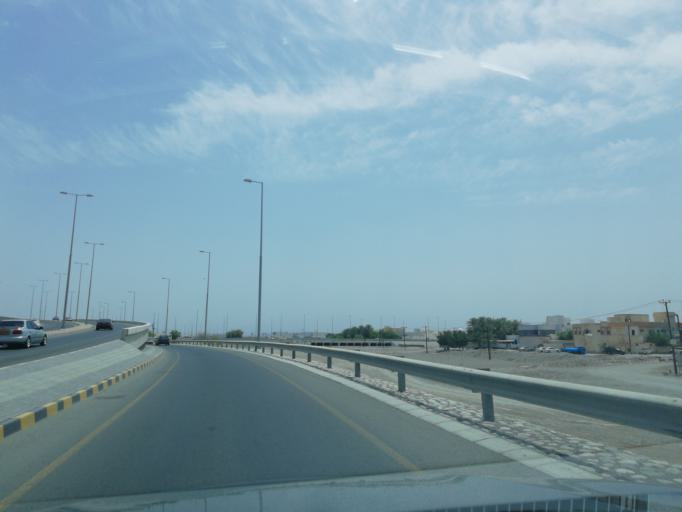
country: OM
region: Muhafazat Masqat
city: As Sib al Jadidah
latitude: 23.6686
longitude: 58.1608
